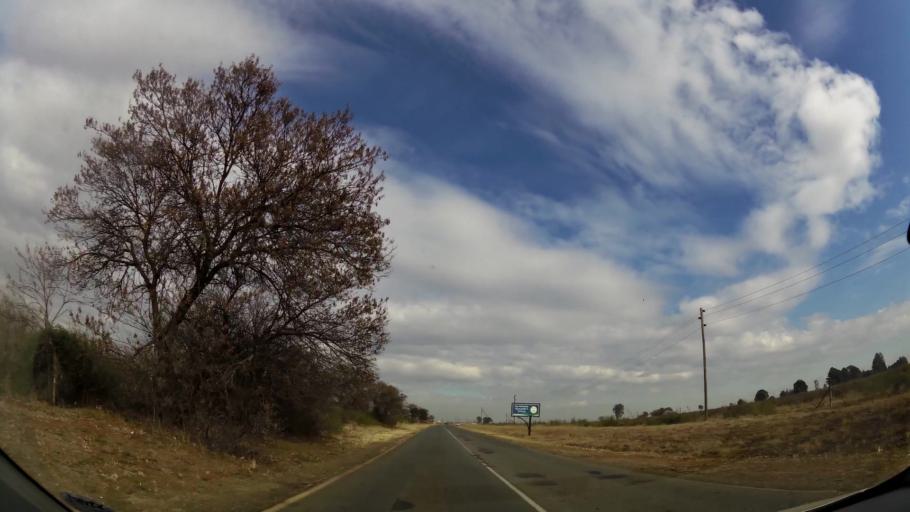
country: ZA
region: Gauteng
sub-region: Sedibeng District Municipality
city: Meyerton
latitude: -26.5580
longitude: 28.0595
